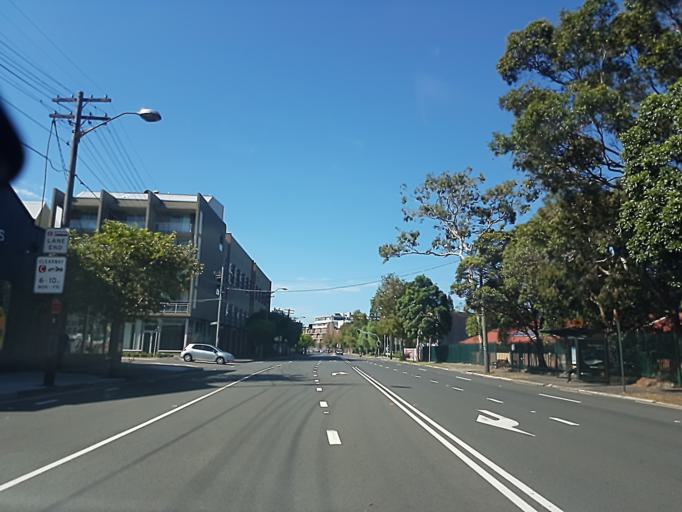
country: AU
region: New South Wales
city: Alexandria
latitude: -33.9201
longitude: 151.1977
